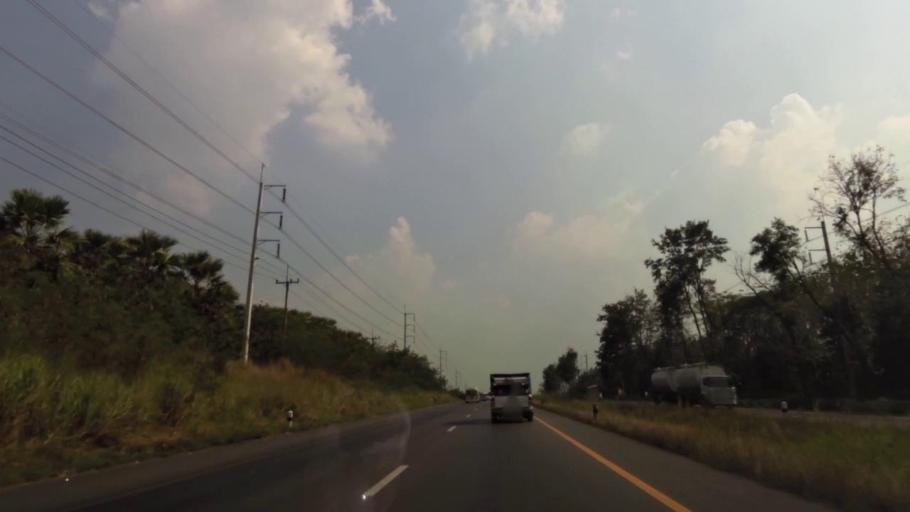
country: TH
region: Chon Buri
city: Nong Yai
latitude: 13.1796
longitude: 101.2643
